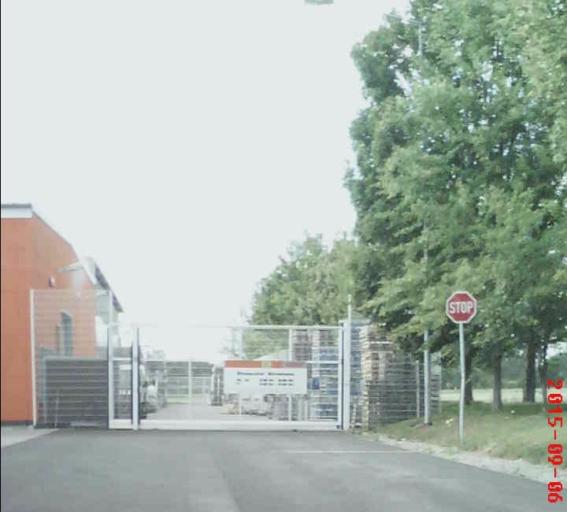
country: DE
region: Thuringia
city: Muehlhausen
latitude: 51.2412
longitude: 10.4584
